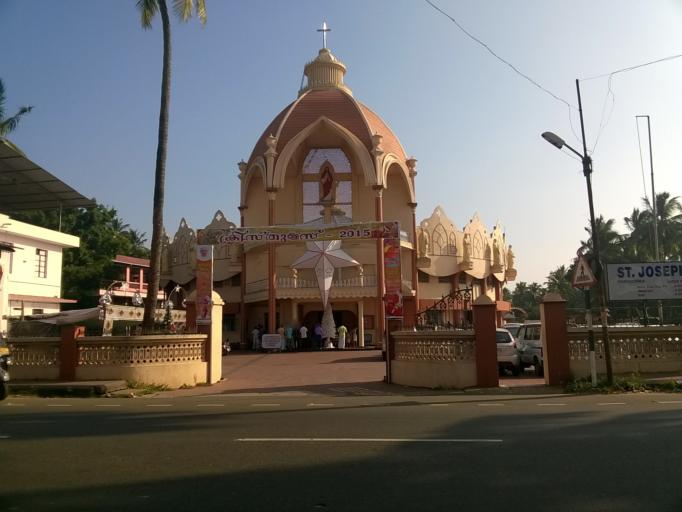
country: IN
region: Kerala
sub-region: Thrissur District
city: Trichur
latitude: 10.5040
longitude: 76.2256
